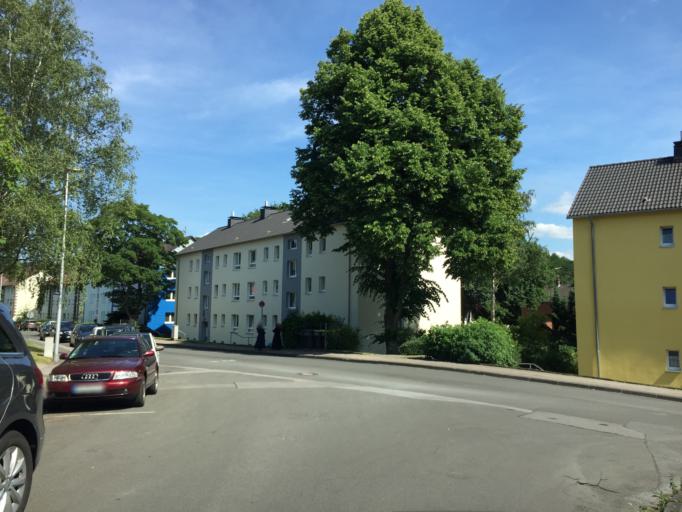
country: DE
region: North Rhine-Westphalia
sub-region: Regierungsbezirk Arnsberg
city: Nachrodt-Wiblingwerde
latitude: 51.3685
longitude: 7.6204
